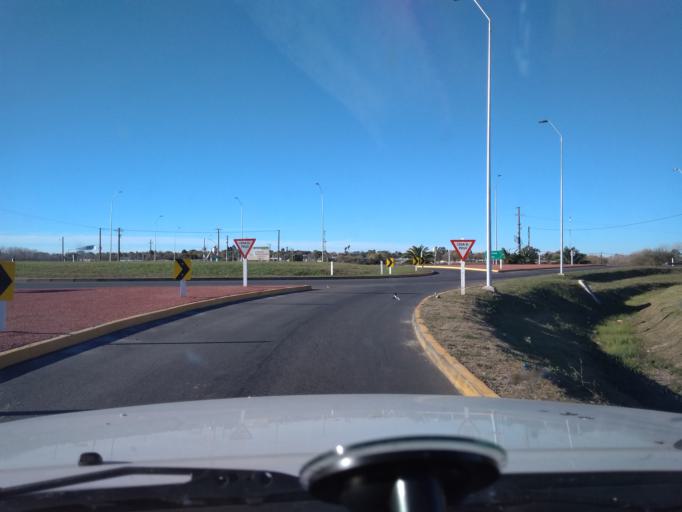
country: UY
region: Canelones
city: Santa Rosa
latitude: -34.5055
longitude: -56.0492
